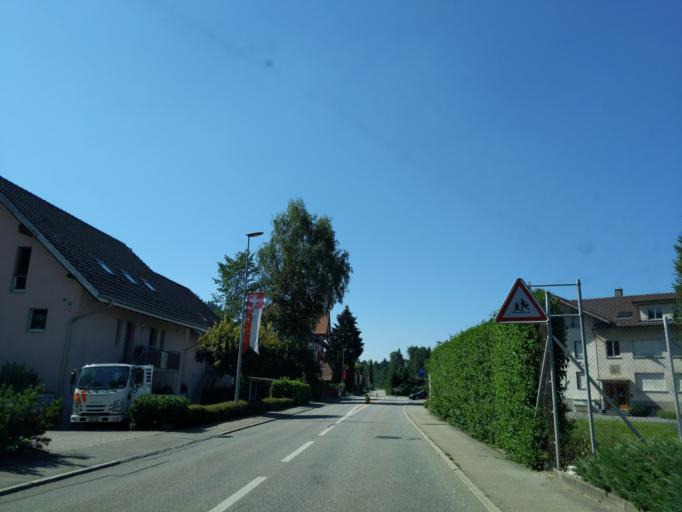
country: CH
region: Bern
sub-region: Emmental District
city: Lauperswil
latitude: 46.9738
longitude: 7.7394
